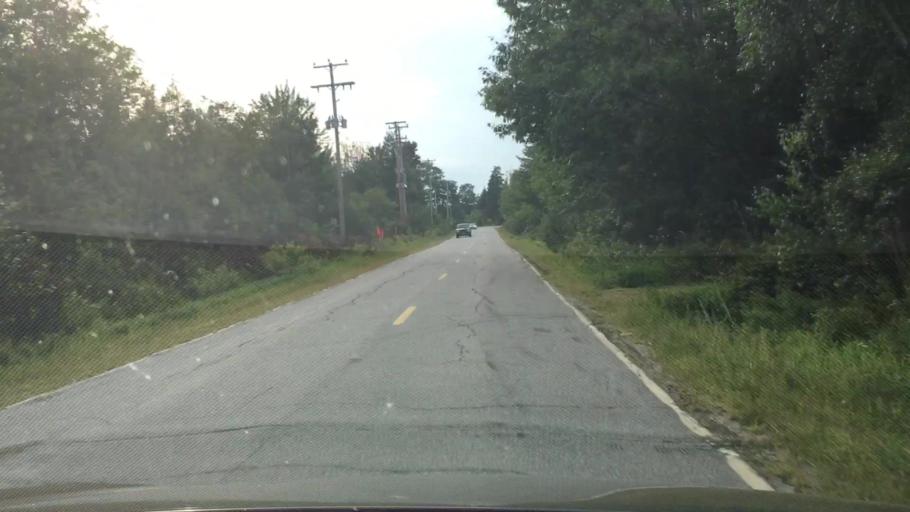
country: US
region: Maine
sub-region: Hancock County
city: Penobscot
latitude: 44.4739
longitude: -68.7763
